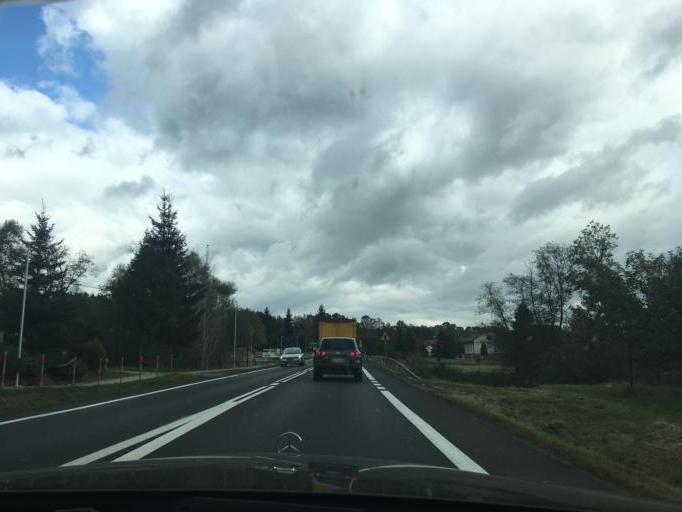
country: PL
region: Subcarpathian Voivodeship
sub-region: Powiat strzyzowski
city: Babica
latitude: 49.9127
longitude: 21.8678
